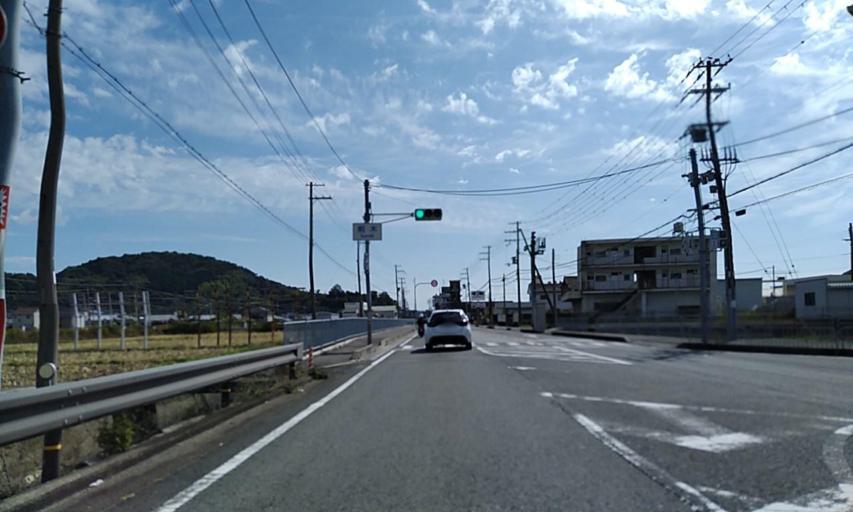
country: JP
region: Wakayama
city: Gobo
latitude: 33.9195
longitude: 135.1465
